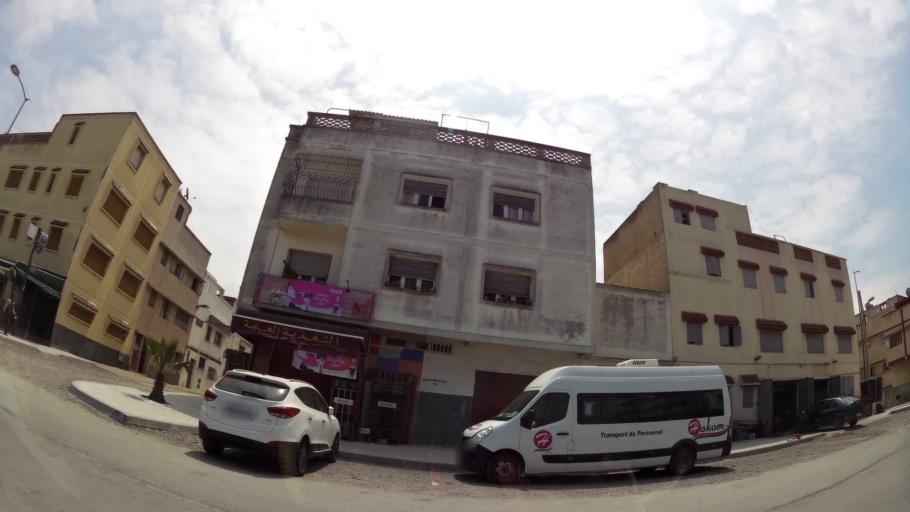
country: MA
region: Rabat-Sale-Zemmour-Zaer
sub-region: Rabat
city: Rabat
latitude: 33.9888
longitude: -6.8803
